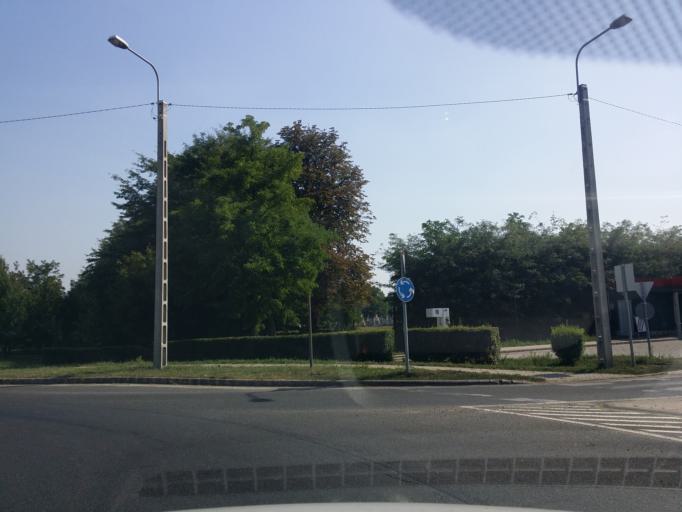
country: HU
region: Fejer
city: Mezofalva
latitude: 46.9302
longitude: 18.7889
